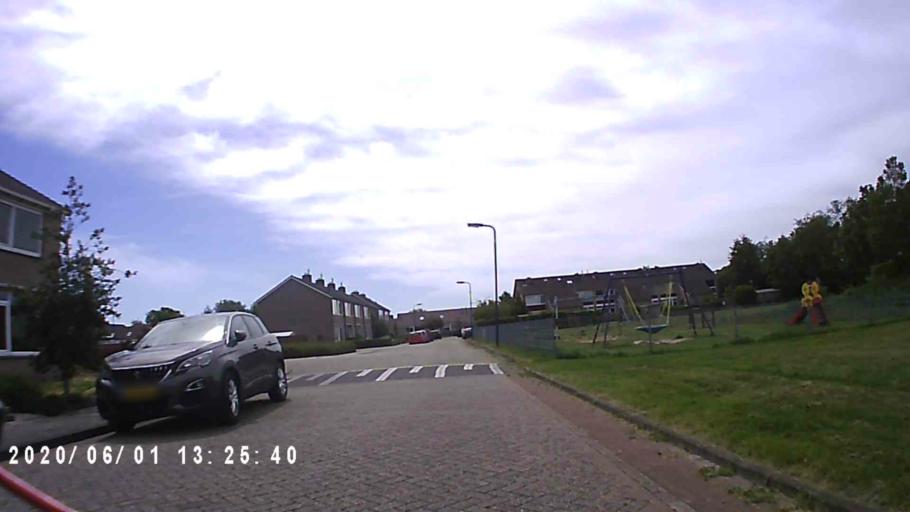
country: NL
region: Friesland
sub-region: Gemeente Littenseradiel
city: Wommels
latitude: 53.1070
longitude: 5.5819
